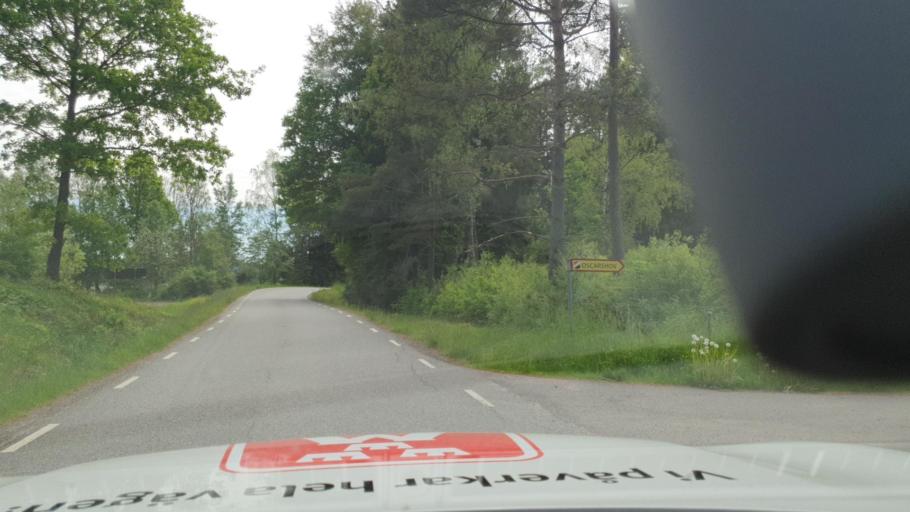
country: SE
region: Vaestra Goetaland
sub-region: Vanersborgs Kommun
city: Vargon
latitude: 58.2697
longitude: 12.5055
